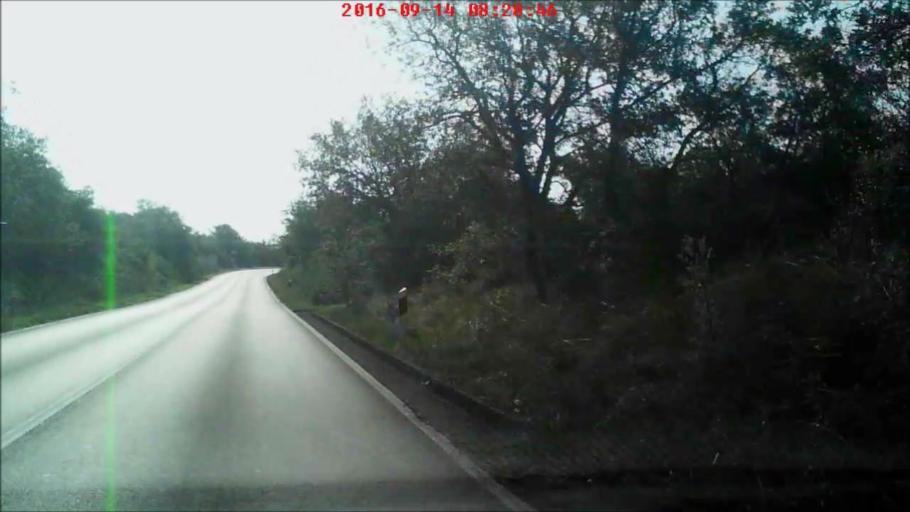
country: HR
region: Zadarska
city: Zadar
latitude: 44.1839
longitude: 15.2786
